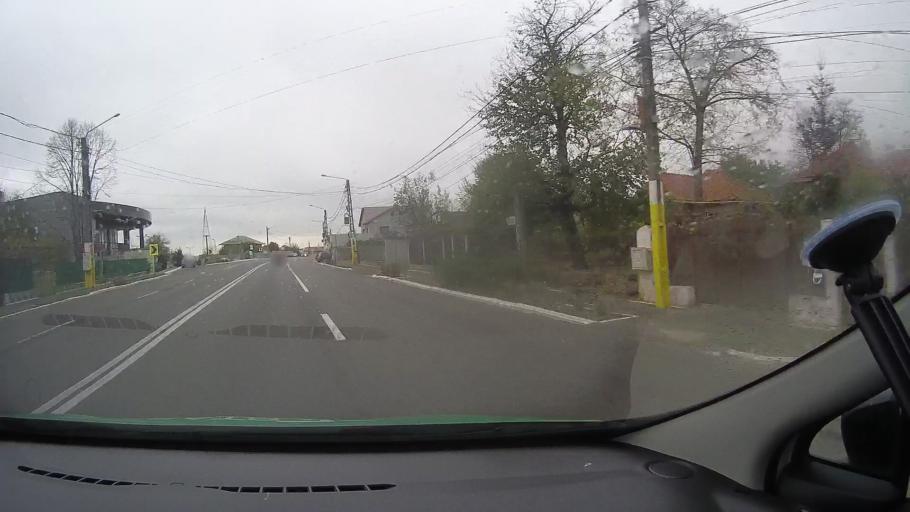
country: RO
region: Constanta
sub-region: Comuna Valu lui Traian
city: Valu lui Traian
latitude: 44.1646
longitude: 28.4737
